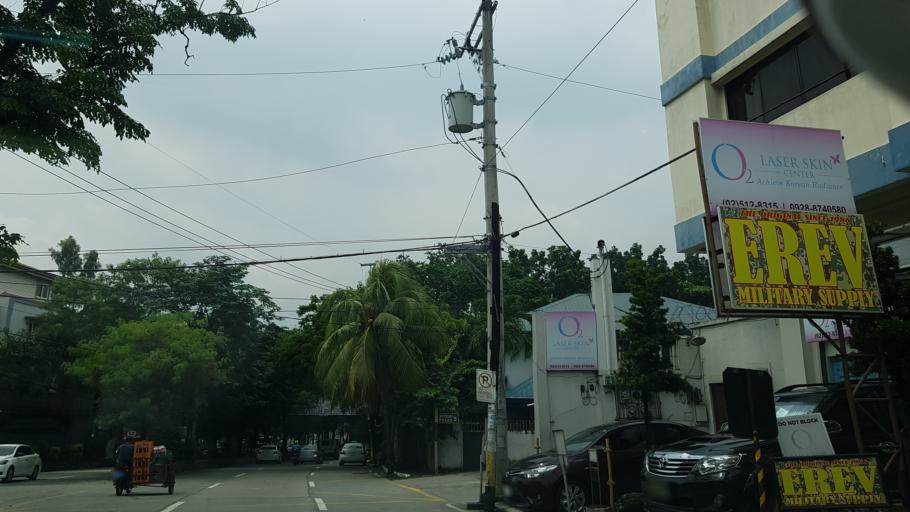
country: PH
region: Metro Manila
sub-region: Makati City
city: Makati City
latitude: 14.5301
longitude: 121.0414
